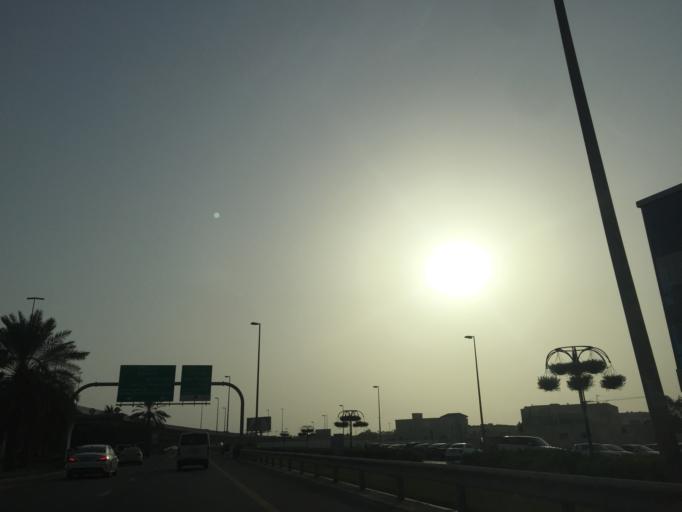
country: AE
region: Dubai
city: Dubai
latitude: 25.1247
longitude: 55.2029
